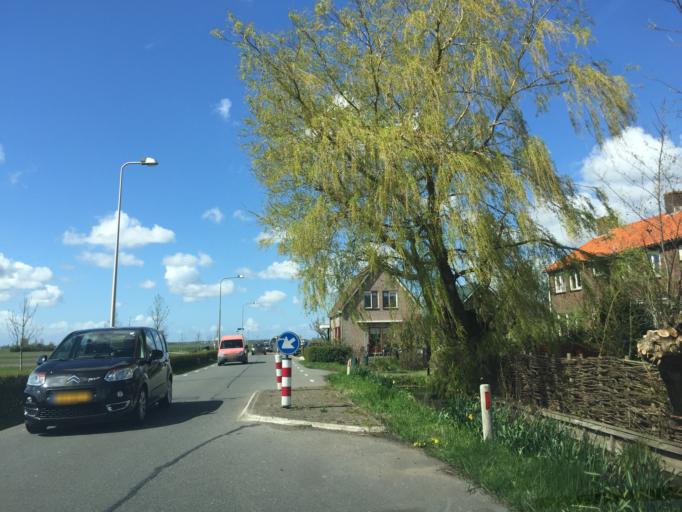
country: NL
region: South Holland
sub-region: Gemeente Kaag en Braassem
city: Leimuiden
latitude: 52.2008
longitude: 4.7217
